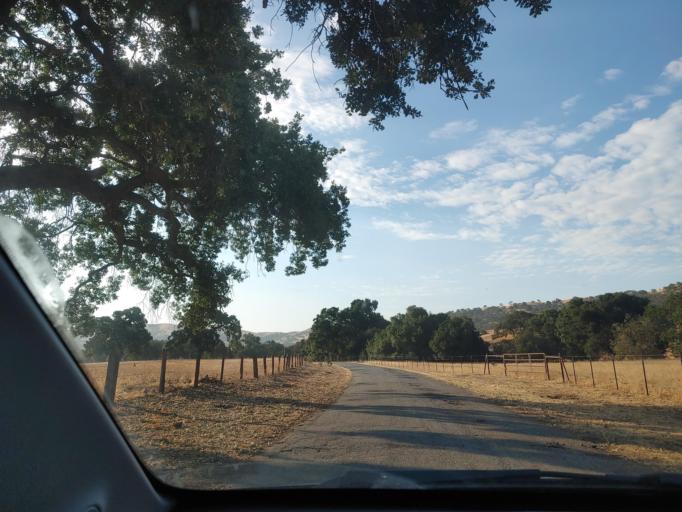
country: US
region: California
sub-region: San Benito County
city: Ridgemark
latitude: 36.7796
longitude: -121.2436
